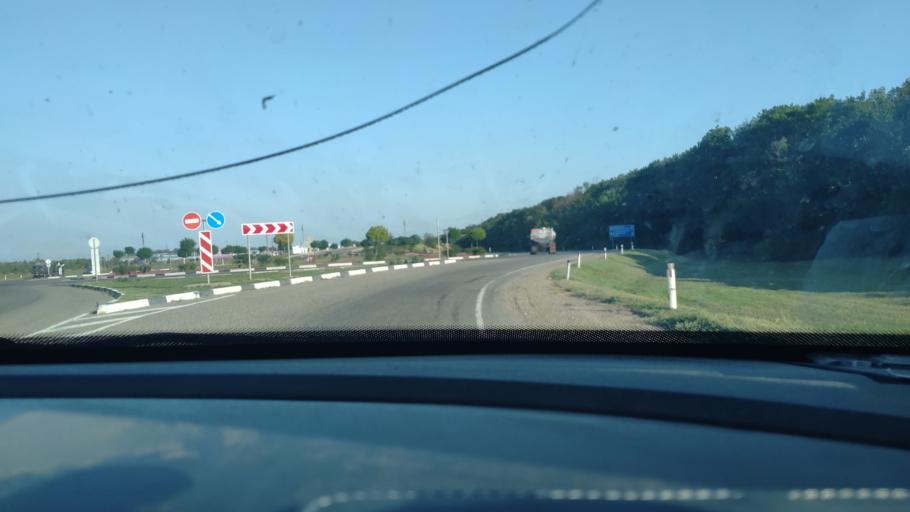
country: RU
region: Krasnodarskiy
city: Starominskaya
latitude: 46.5260
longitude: 39.0084
